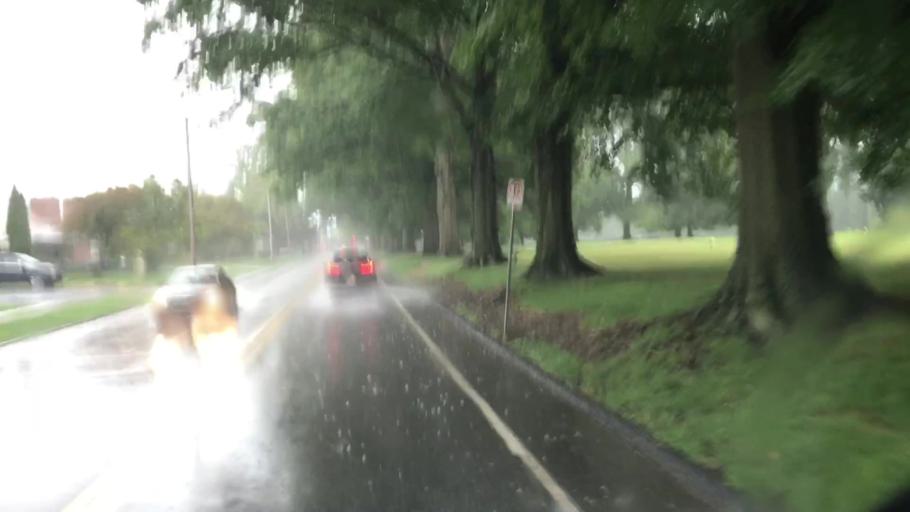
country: US
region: Pennsylvania
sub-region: Cumberland County
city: Camp Hill
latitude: 40.2300
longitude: -76.9127
